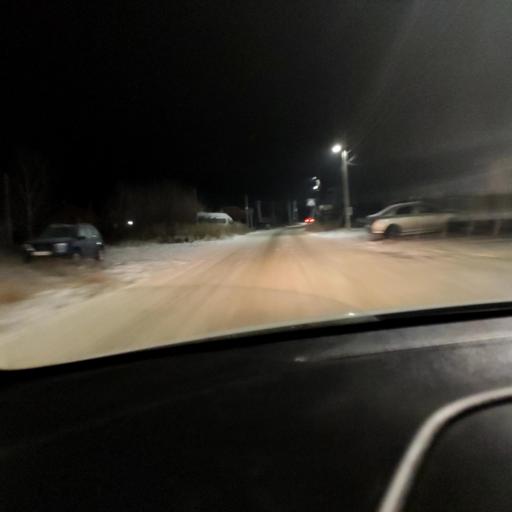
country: RU
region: Tatarstan
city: Staroye Arakchino
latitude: 55.8841
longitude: 49.0396
